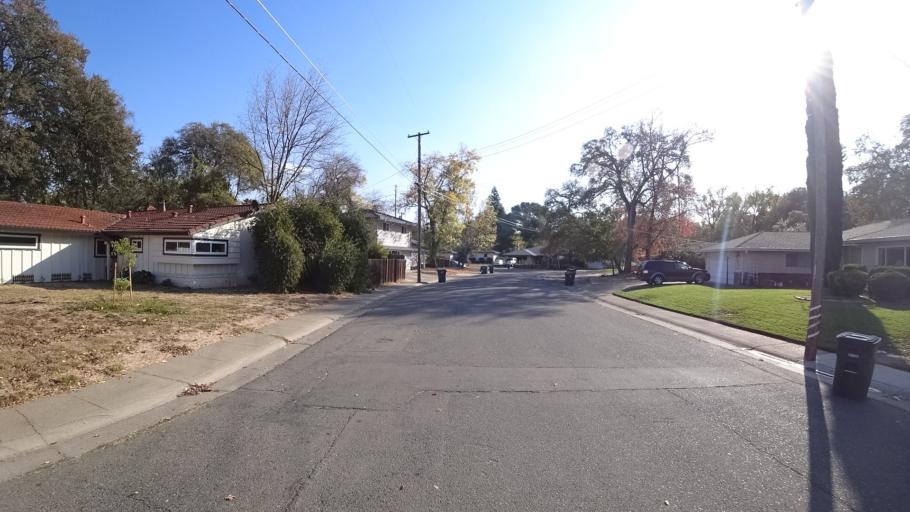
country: US
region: California
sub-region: Sacramento County
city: Citrus Heights
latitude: 38.6866
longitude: -121.2798
